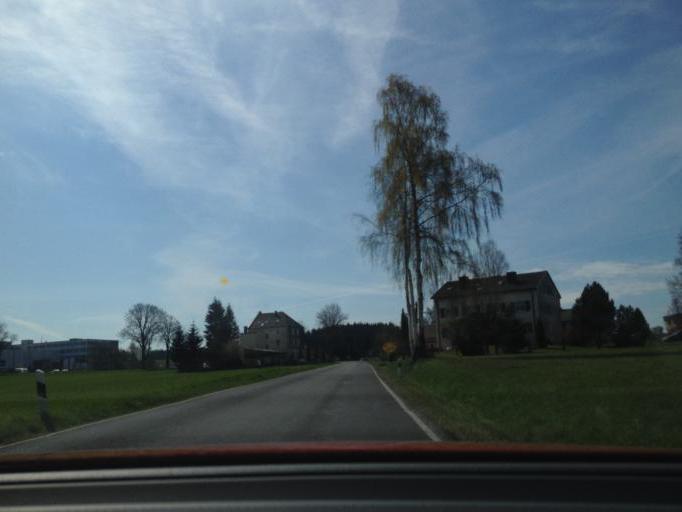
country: DE
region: Bavaria
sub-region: Upper Franconia
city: Roslau
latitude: 50.0807
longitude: 11.9818
